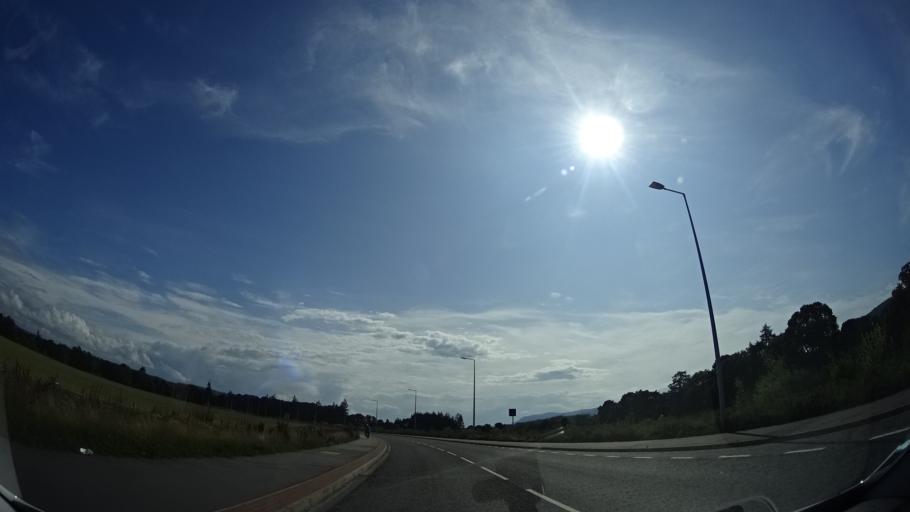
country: GB
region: Scotland
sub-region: Highland
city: Inverness
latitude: 57.4556
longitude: -4.2556
